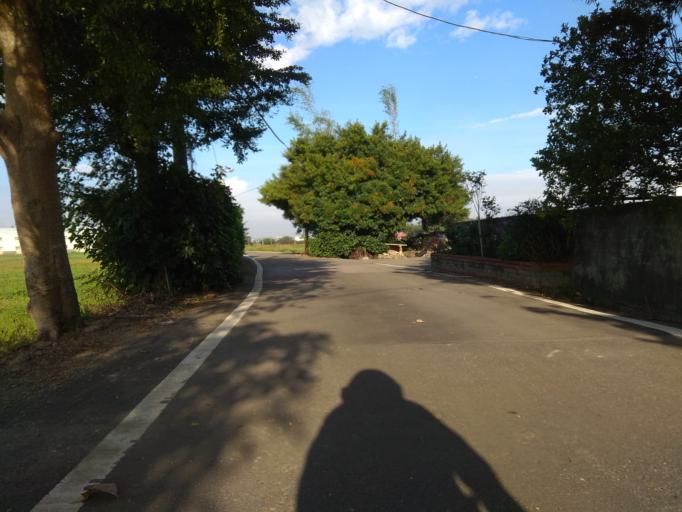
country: TW
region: Taiwan
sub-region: Hsinchu
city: Zhubei
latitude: 24.9769
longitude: 121.0598
